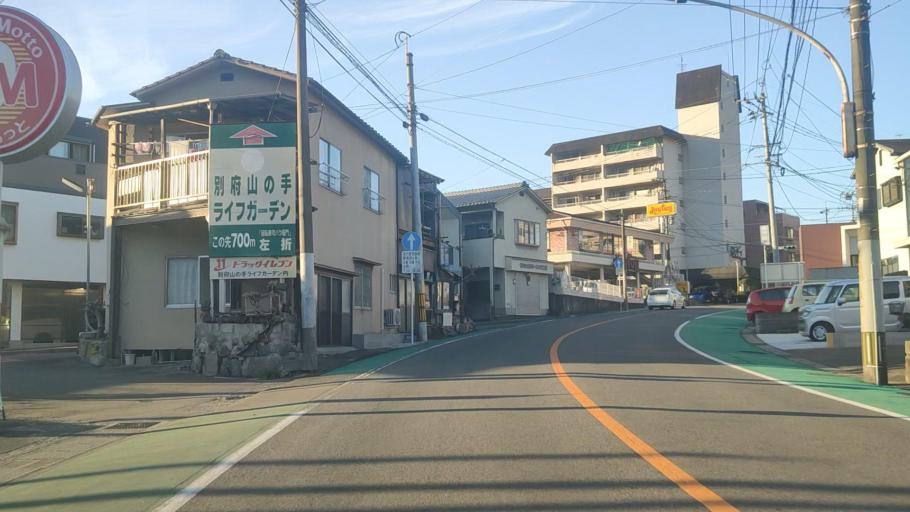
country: JP
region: Oita
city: Beppu
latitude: 33.2777
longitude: 131.4896
